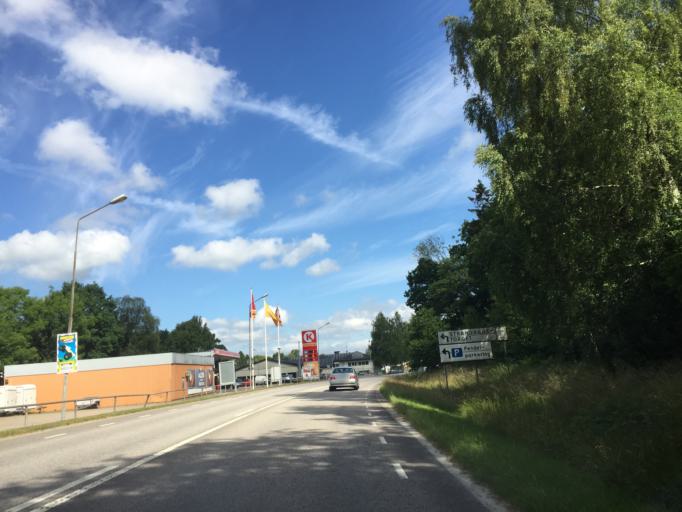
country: SE
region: Vaestra Goetaland
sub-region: Orust
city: Henan
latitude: 58.2319
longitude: 11.6824
